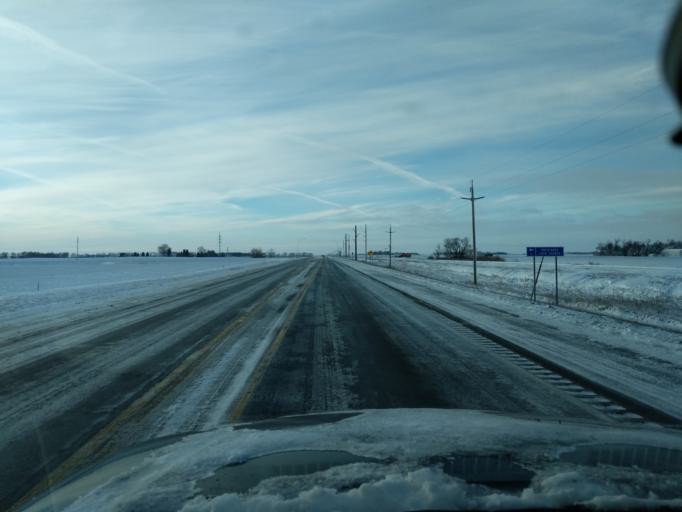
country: US
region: Minnesota
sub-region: Renville County
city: Hector
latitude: 44.7504
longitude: -94.7673
